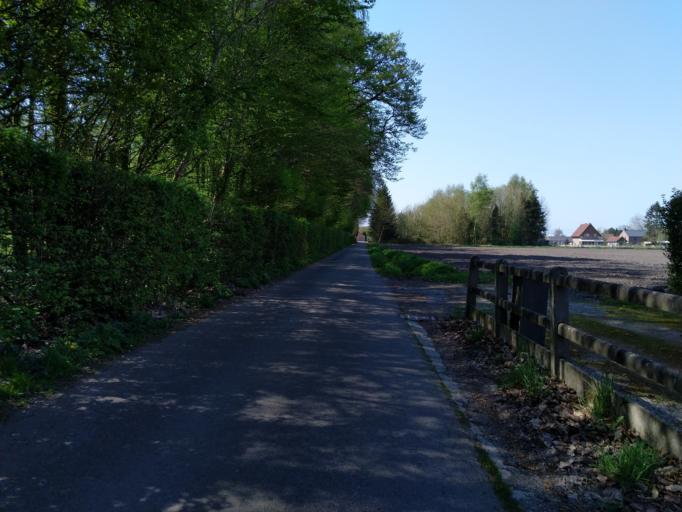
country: BE
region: Wallonia
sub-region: Province du Hainaut
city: Jurbise
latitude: 50.5146
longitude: 3.9268
